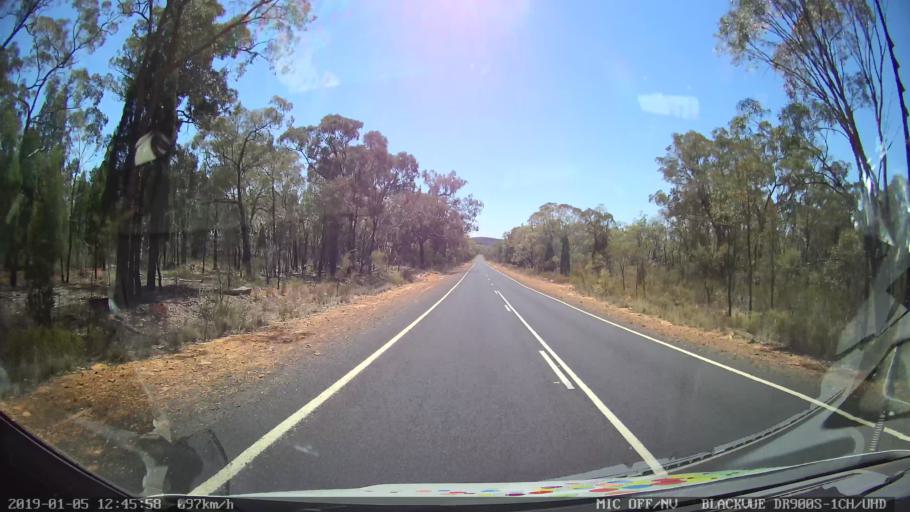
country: AU
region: New South Wales
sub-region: Warrumbungle Shire
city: Coonabarabran
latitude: -31.1227
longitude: 149.5565
